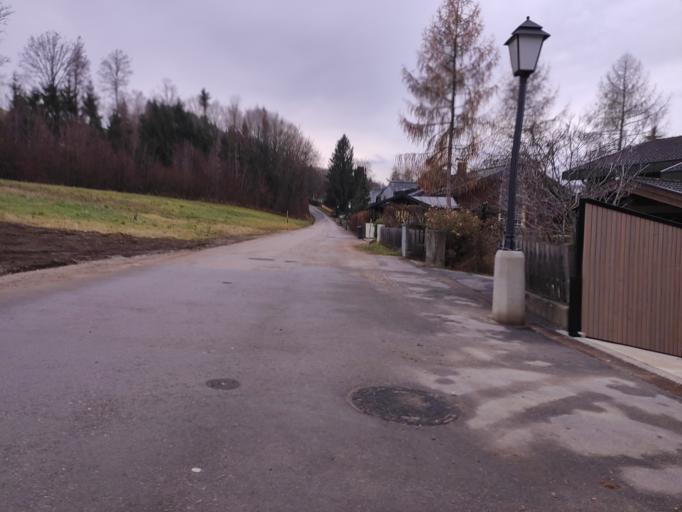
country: AT
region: Salzburg
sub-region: Politischer Bezirk Salzburg-Umgebung
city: Mattsee
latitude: 47.9652
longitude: 13.0967
